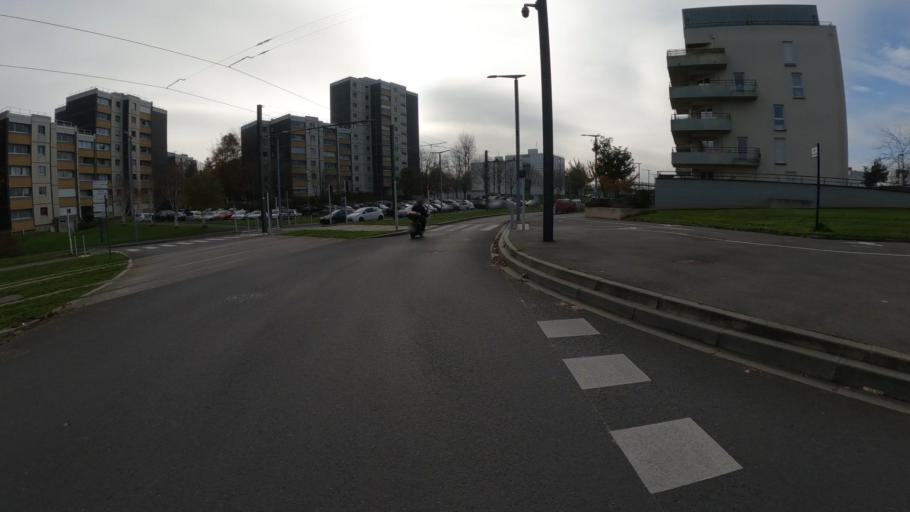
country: FR
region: Lower Normandy
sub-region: Departement du Calvados
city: Caen
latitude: 49.2026
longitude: -0.3413
